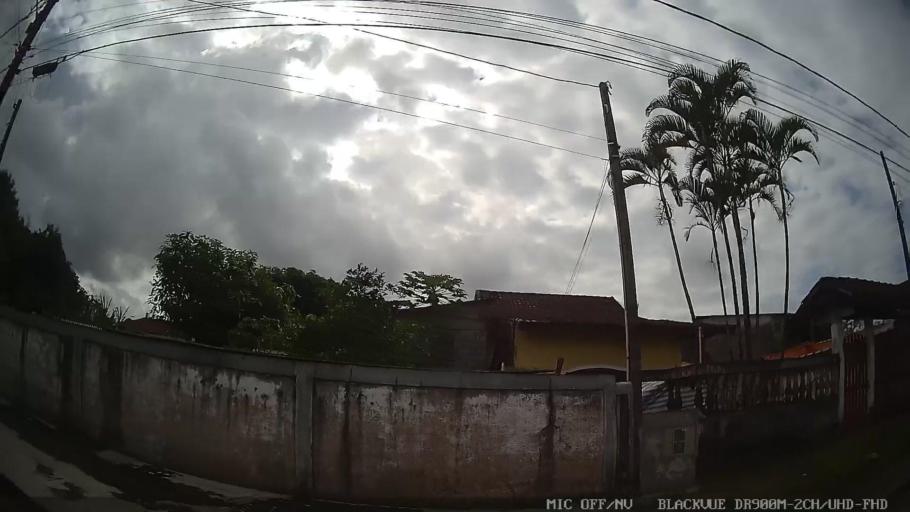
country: BR
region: Sao Paulo
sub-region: Itanhaem
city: Itanhaem
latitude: -24.1962
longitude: -46.8202
